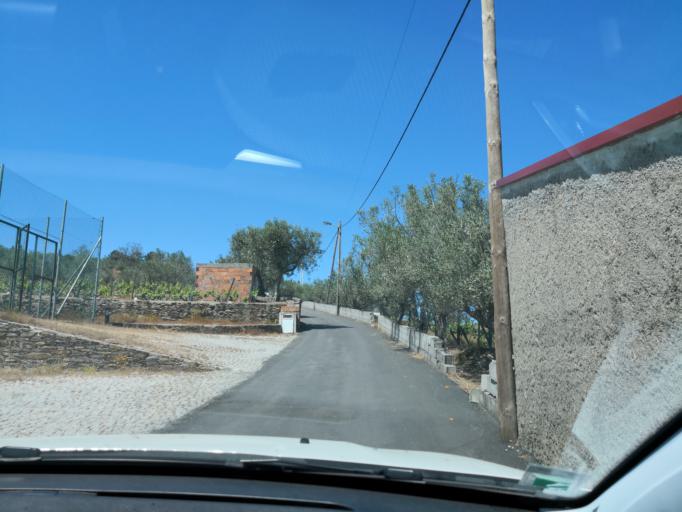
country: PT
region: Vila Real
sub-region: Vila Real
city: Vila Real
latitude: 41.2292
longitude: -7.7294
